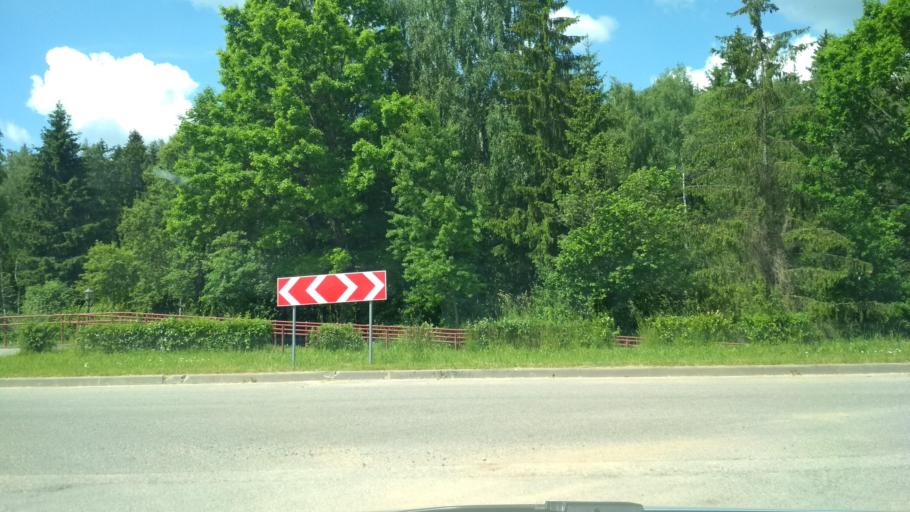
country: BY
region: Grodnenskaya
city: Astravyets
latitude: 54.6180
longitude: 25.9776
